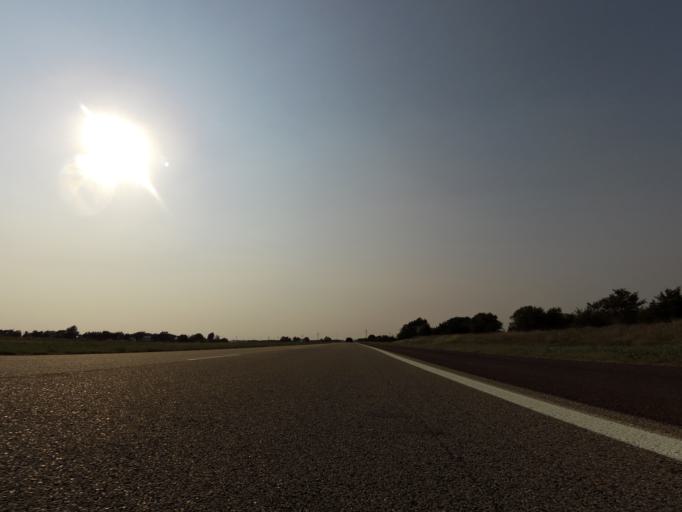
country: US
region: Kansas
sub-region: Reno County
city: South Hutchinson
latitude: 37.9531
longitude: -97.8977
